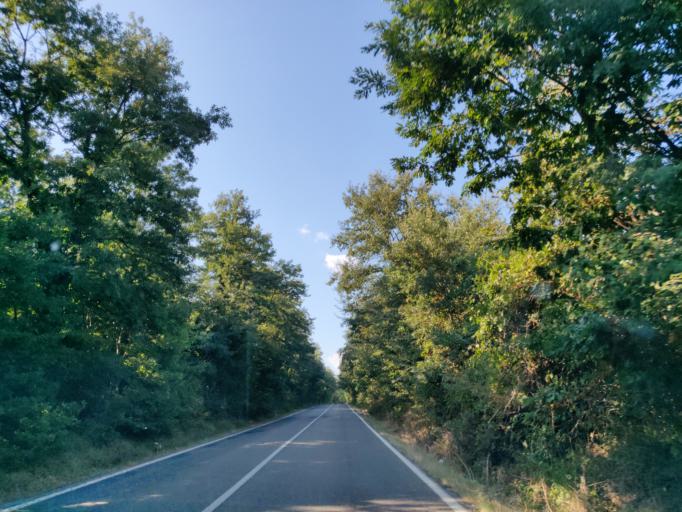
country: IT
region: Latium
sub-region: Provincia di Viterbo
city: Latera
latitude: 42.6081
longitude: 11.8435
